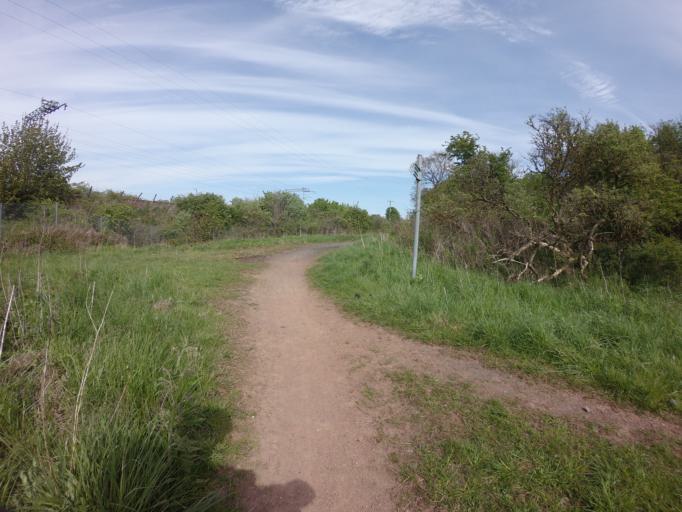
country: GB
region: Scotland
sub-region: West Lothian
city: Broxburn
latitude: 55.9197
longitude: -3.4912
